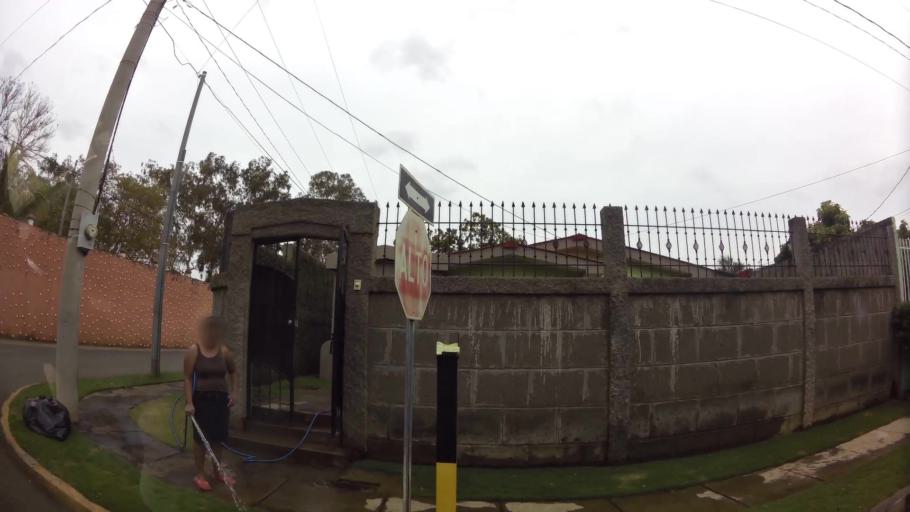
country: NI
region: Masaya
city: Ticuantepe
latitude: 12.0636
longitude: -86.1850
